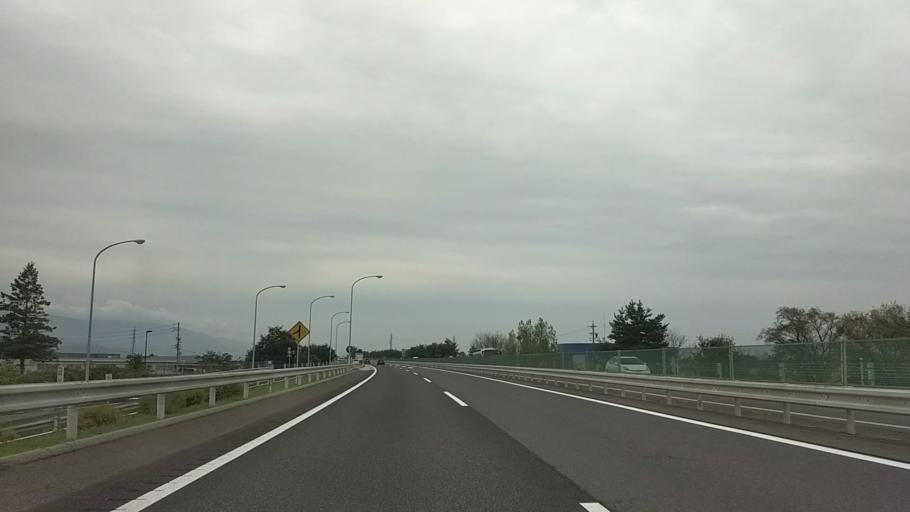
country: JP
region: Nagano
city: Toyoshina
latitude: 36.2700
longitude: 137.9312
